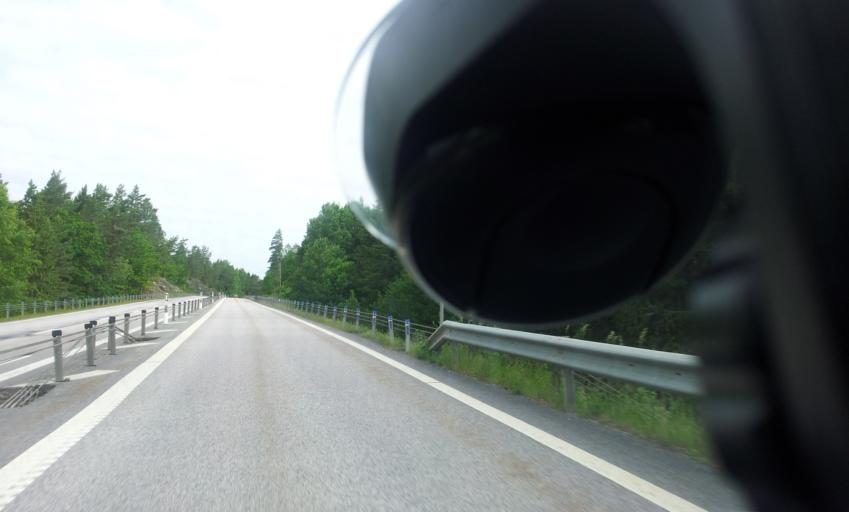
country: SE
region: Kalmar
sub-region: Vasterviks Kommun
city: Forserum
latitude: 58.0245
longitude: 16.5186
